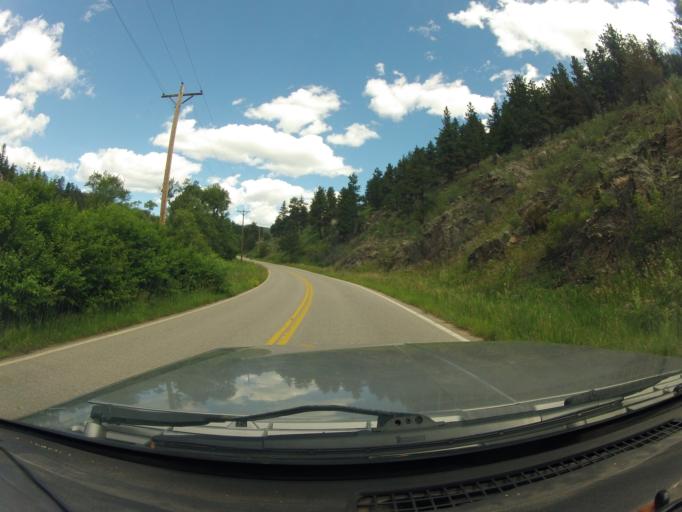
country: US
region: Colorado
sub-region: Larimer County
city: Laporte
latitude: 40.5733
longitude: -105.3235
